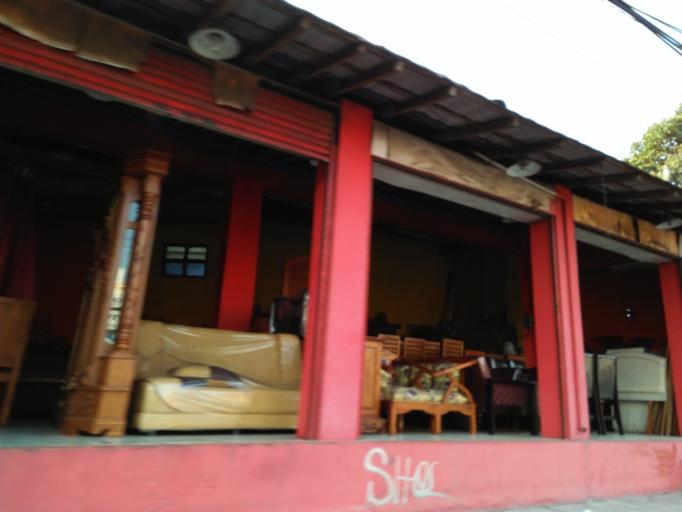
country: ID
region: Daerah Istimewa Yogyakarta
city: Depok
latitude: -7.7805
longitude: 110.4525
